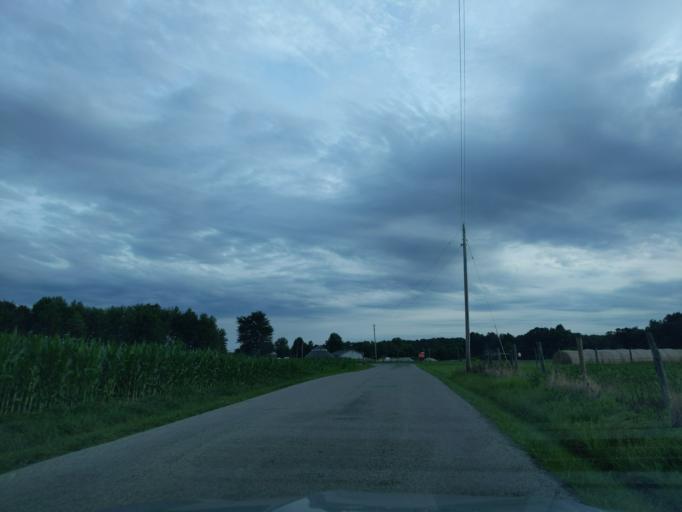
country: US
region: Indiana
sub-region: Ripley County
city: Sunman
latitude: 39.2864
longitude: -85.1004
